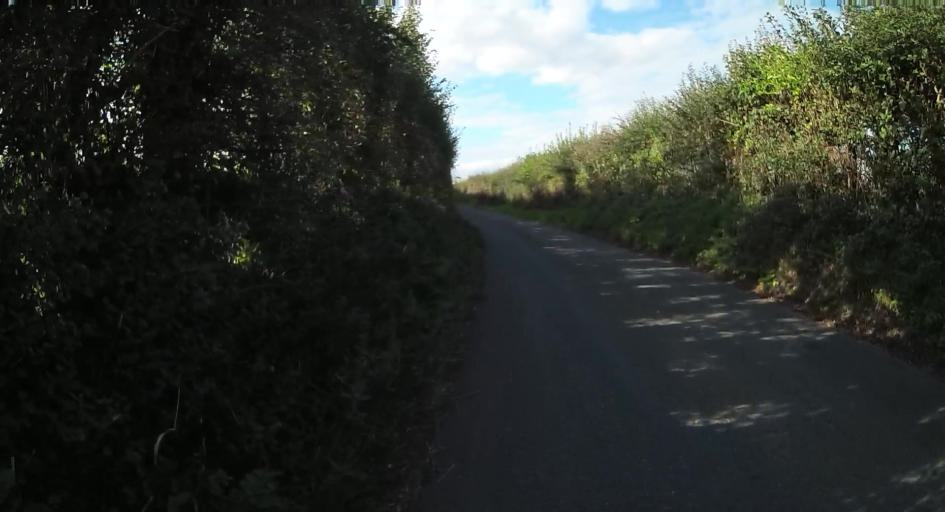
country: GB
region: England
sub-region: Isle of Wight
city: Chale
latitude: 50.6459
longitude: -1.2976
